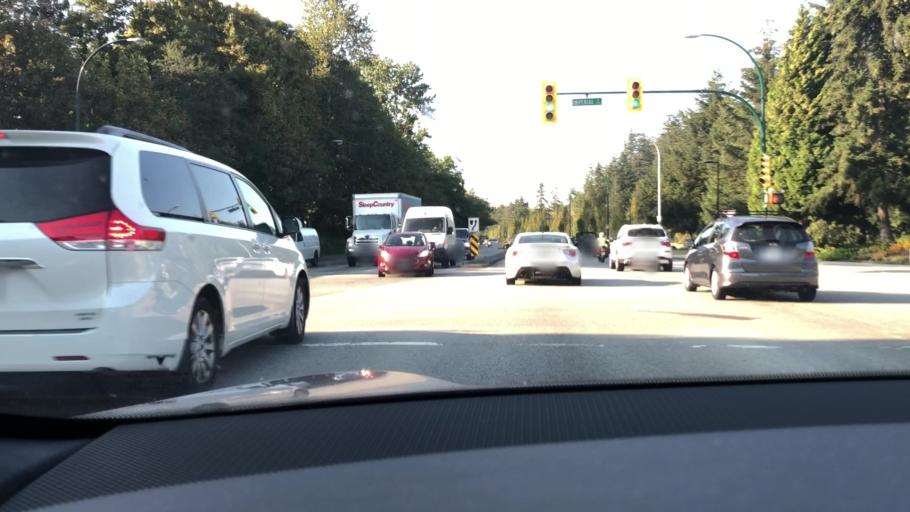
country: CA
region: British Columbia
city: Burnaby
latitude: 49.2218
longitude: -123.0236
